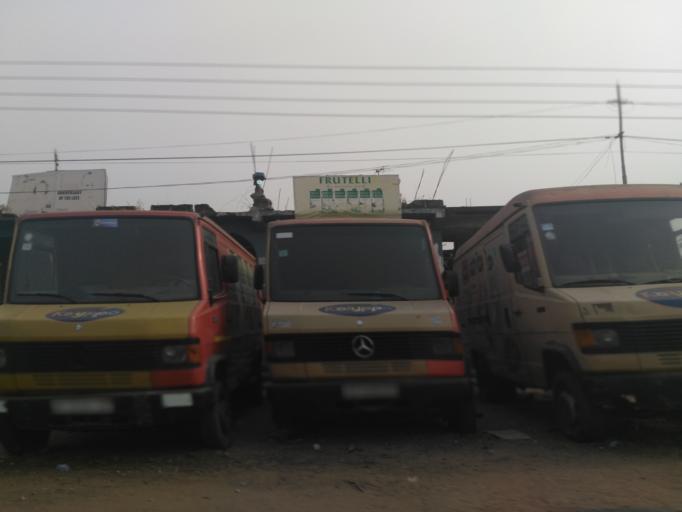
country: GH
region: Ashanti
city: Tafo
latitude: 6.7129
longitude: -1.6198
